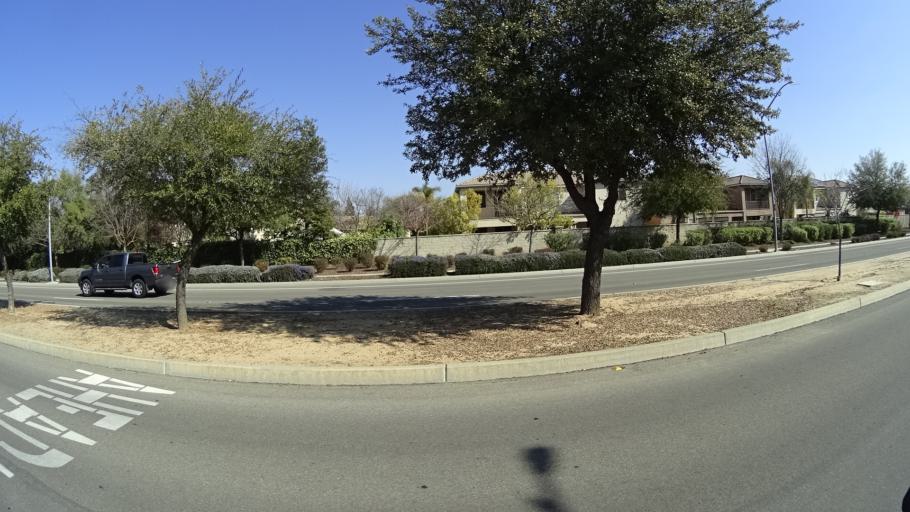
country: US
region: California
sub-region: Fresno County
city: Clovis
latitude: 36.8759
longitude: -119.7438
